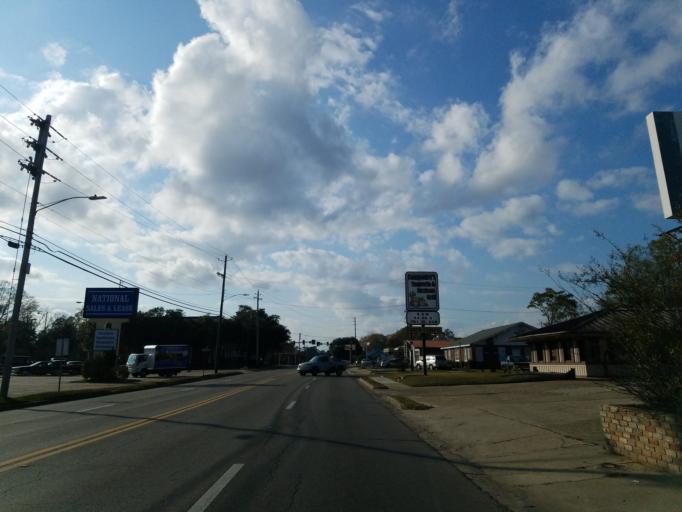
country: US
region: Mississippi
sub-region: Forrest County
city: Hattiesburg
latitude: 31.3248
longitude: -89.3083
